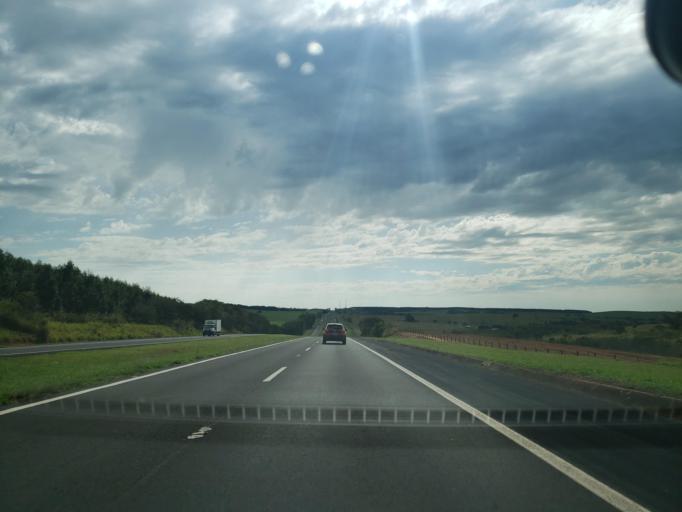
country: BR
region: Sao Paulo
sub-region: Cafelandia
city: Cafelandia
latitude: -21.7874
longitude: -49.6531
